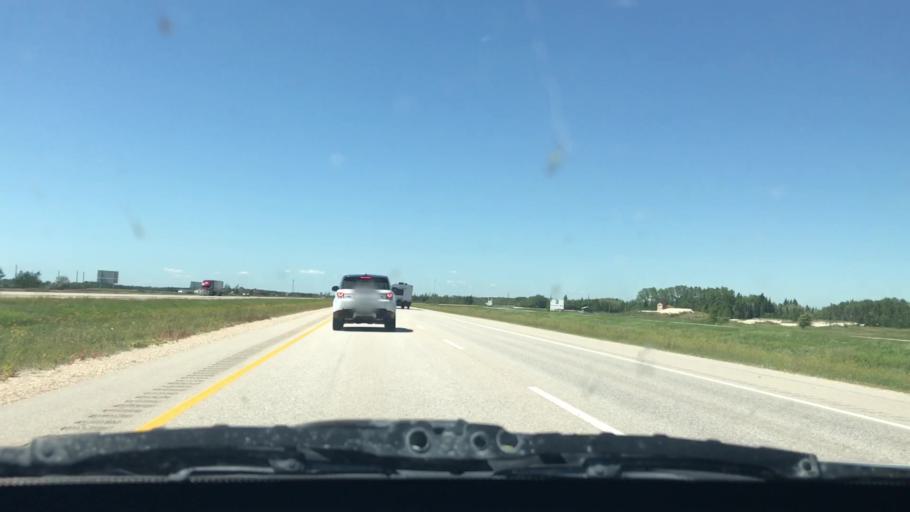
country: CA
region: Manitoba
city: Niverville
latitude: 49.8084
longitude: -96.9069
